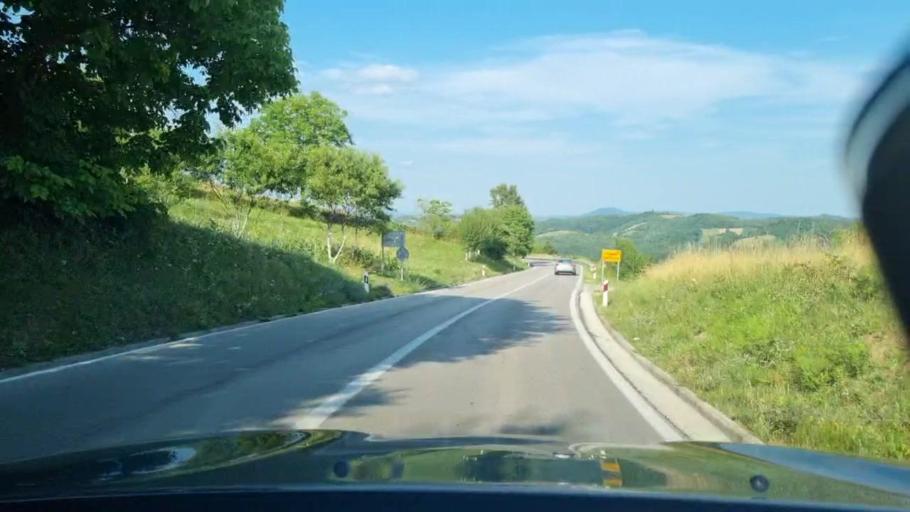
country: BA
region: Federation of Bosnia and Herzegovina
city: Skokovi
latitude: 45.0341
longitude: 15.9152
